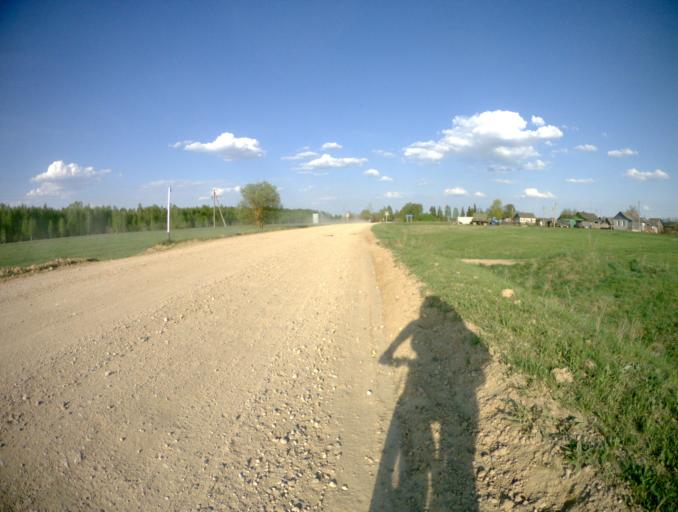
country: RU
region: Vladimir
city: Mstera
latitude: 56.5522
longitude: 41.6995
